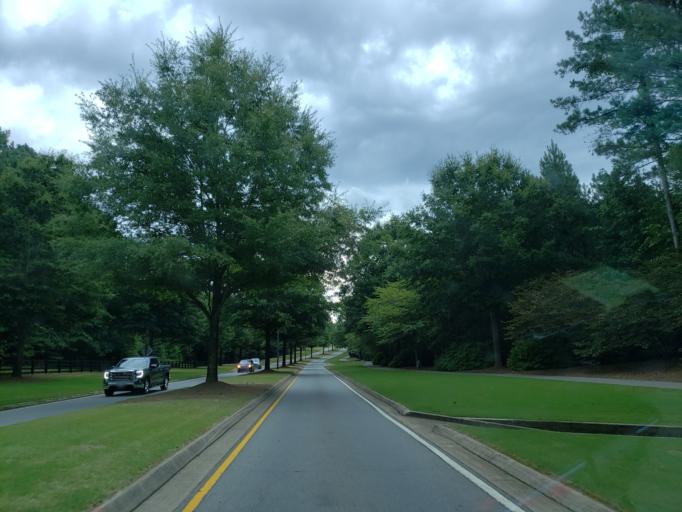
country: US
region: Georgia
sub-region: Bartow County
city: Emerson
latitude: 34.0259
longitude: -84.7814
